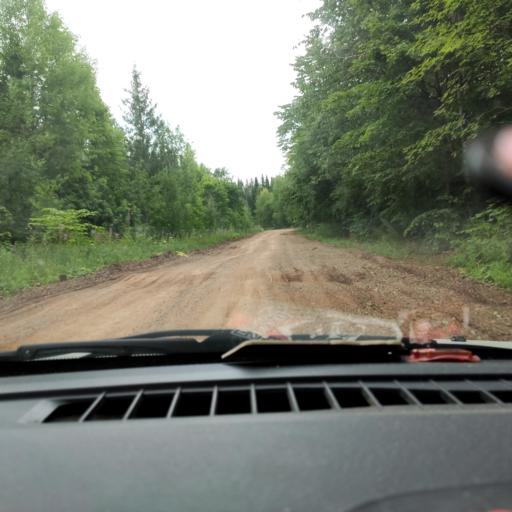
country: RU
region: Perm
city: Kultayevo
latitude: 57.8096
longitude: 56.0039
